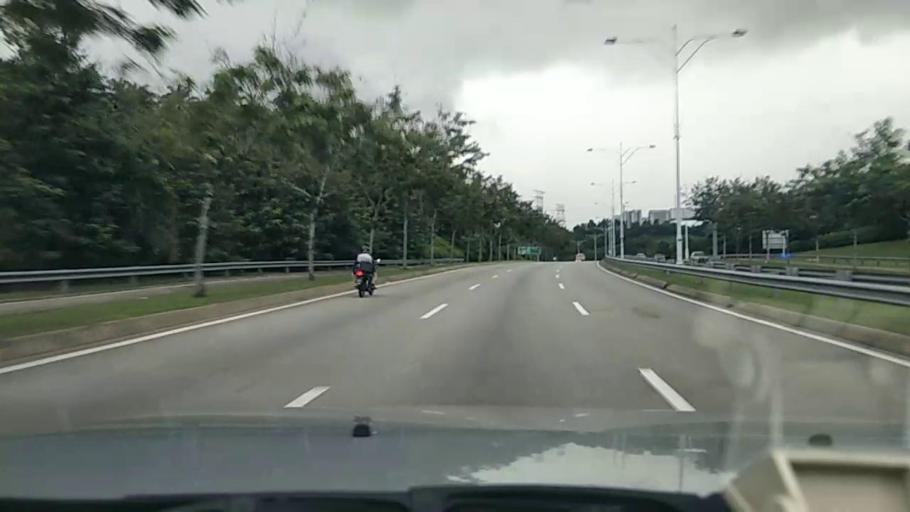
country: MY
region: Putrajaya
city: Putrajaya
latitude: 2.9503
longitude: 101.7134
